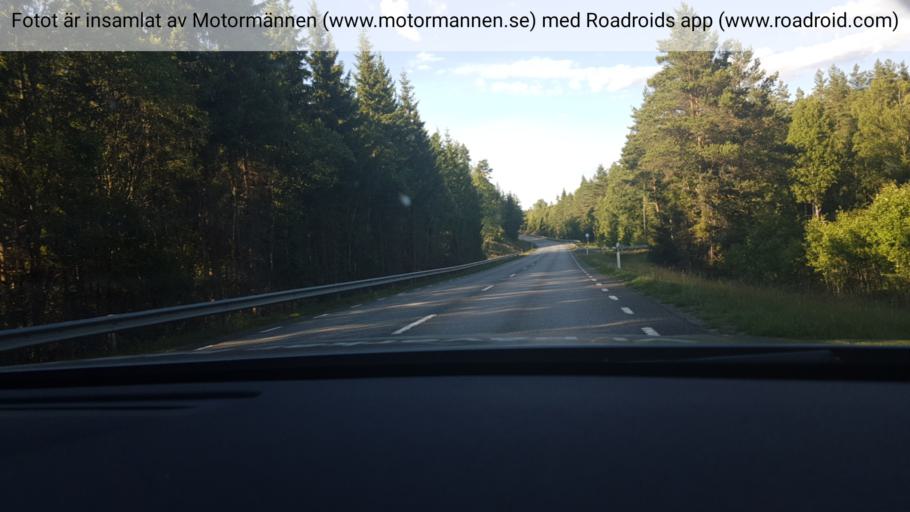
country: SE
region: Joenkoeping
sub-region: Jonkopings Kommun
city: Taberg
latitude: 57.6769
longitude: 13.8440
